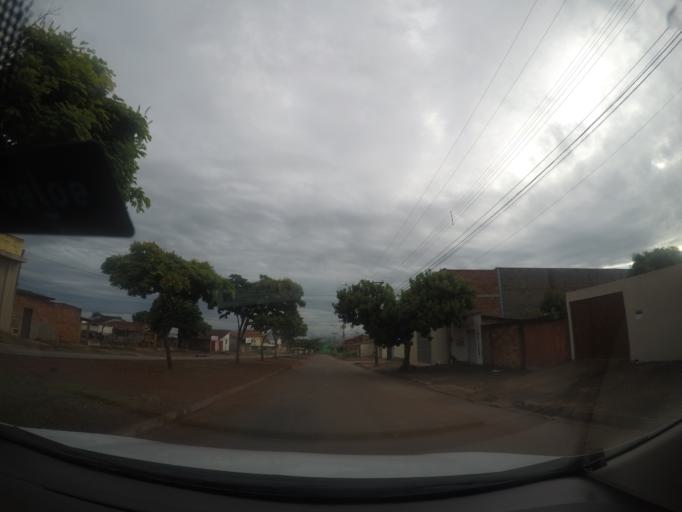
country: BR
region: Goias
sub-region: Goiania
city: Goiania
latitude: -16.6068
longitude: -49.3131
